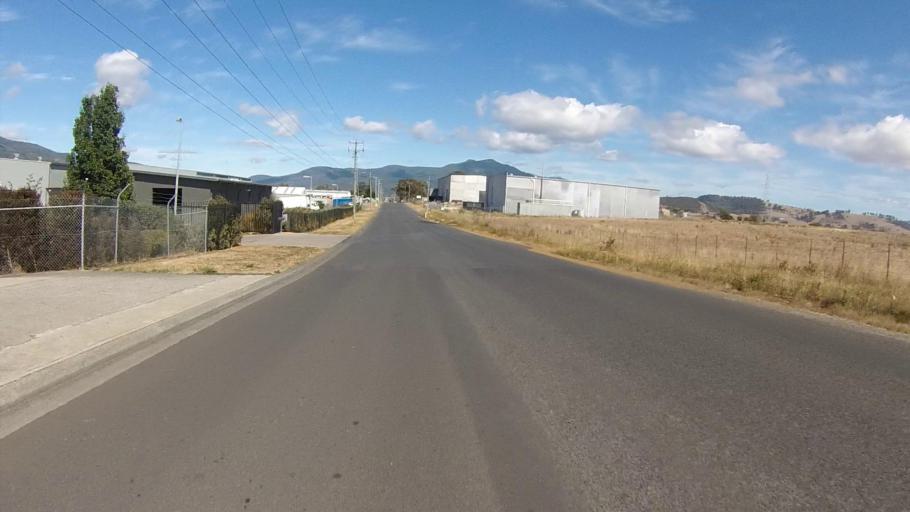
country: AU
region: Tasmania
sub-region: Brighton
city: Bridgewater
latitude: -42.7345
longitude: 147.2506
